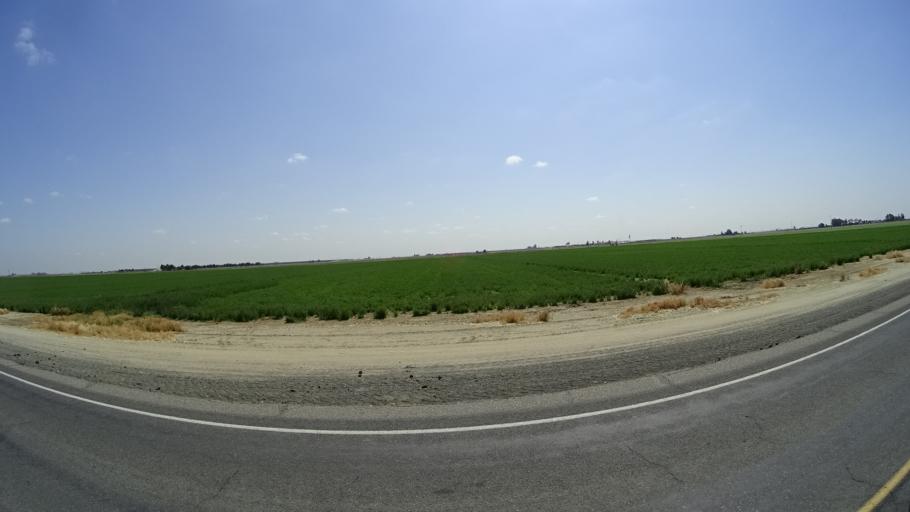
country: US
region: California
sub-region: Kings County
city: Home Garden
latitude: 36.2346
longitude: -119.6369
